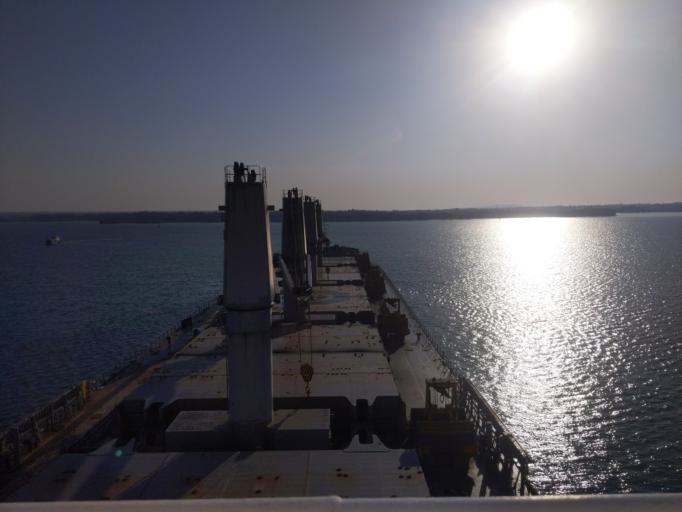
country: ZA
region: KwaZulu-Natal
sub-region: uThungulu District Municipality
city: Richards Bay
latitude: -28.8042
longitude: 32.0530
